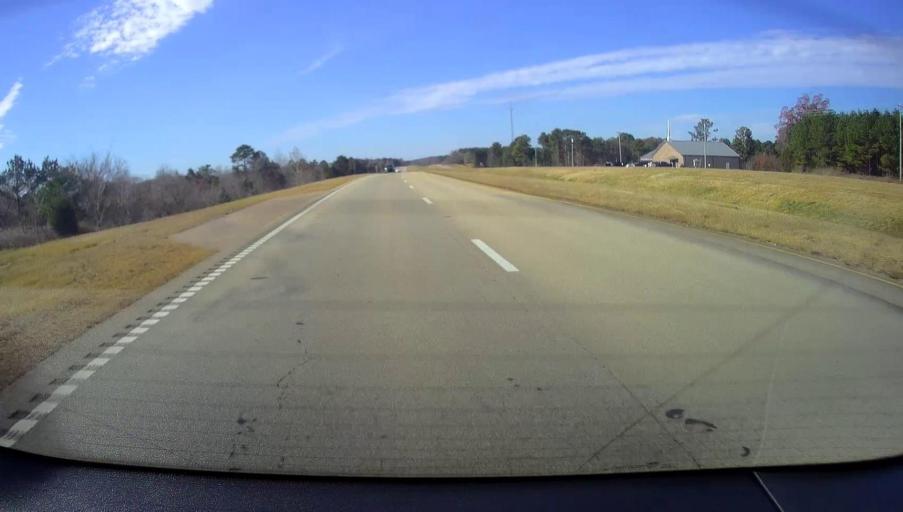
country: US
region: Mississippi
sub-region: Benton County
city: Ashland
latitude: 34.9529
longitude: -89.0071
